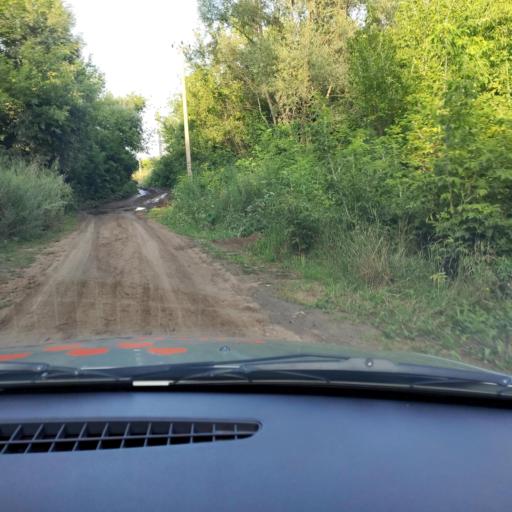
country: RU
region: Bashkortostan
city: Ufa
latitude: 54.6094
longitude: 55.9560
